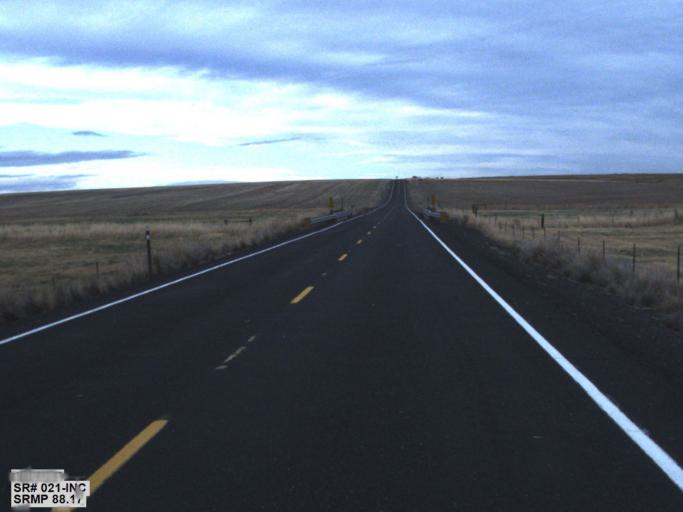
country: US
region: Washington
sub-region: Okanogan County
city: Coulee Dam
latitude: 47.7149
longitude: -118.7221
